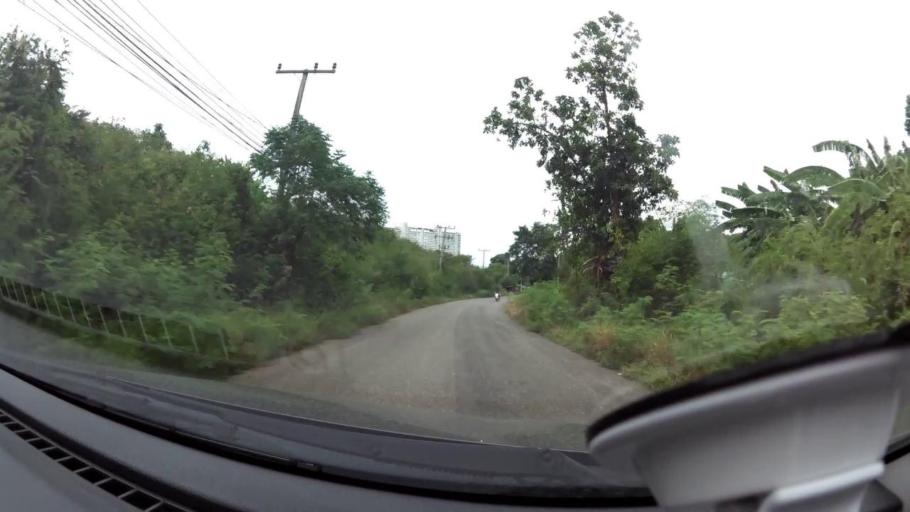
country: TH
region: Prachuap Khiri Khan
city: Pran Buri
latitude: 12.4370
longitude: 99.9733
